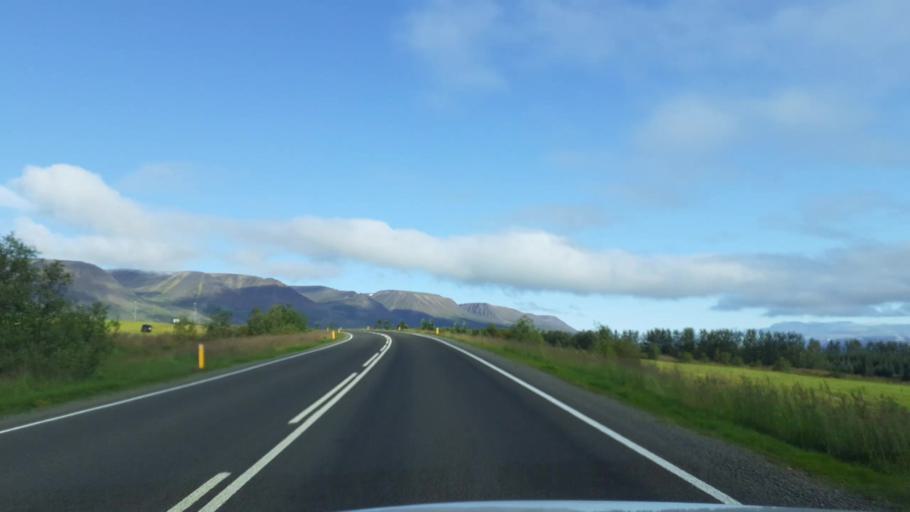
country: IS
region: Northeast
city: Akureyri
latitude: 65.7423
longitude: -18.1987
